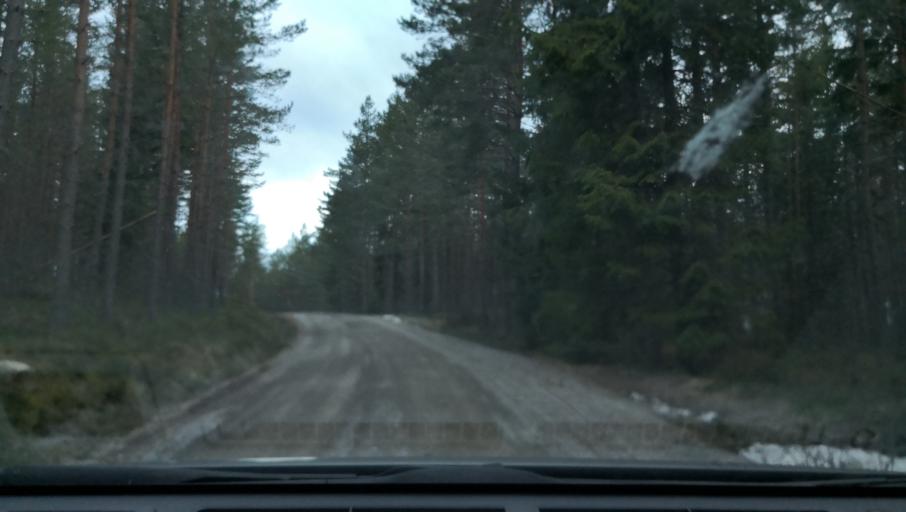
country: SE
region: Vaestmanland
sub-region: Kopings Kommun
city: Kolsva
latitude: 59.5673
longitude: 15.8162
